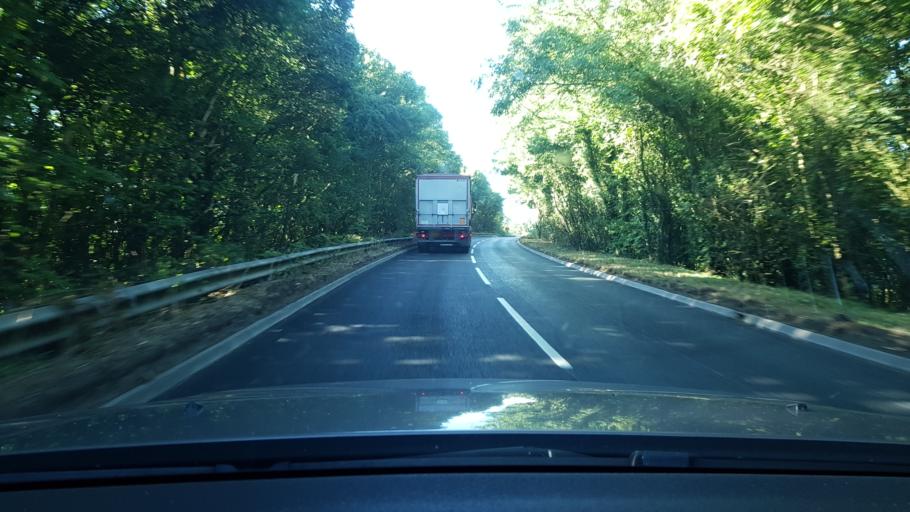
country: GB
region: England
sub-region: West Berkshire
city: Lambourn
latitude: 51.4811
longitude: -1.5503
